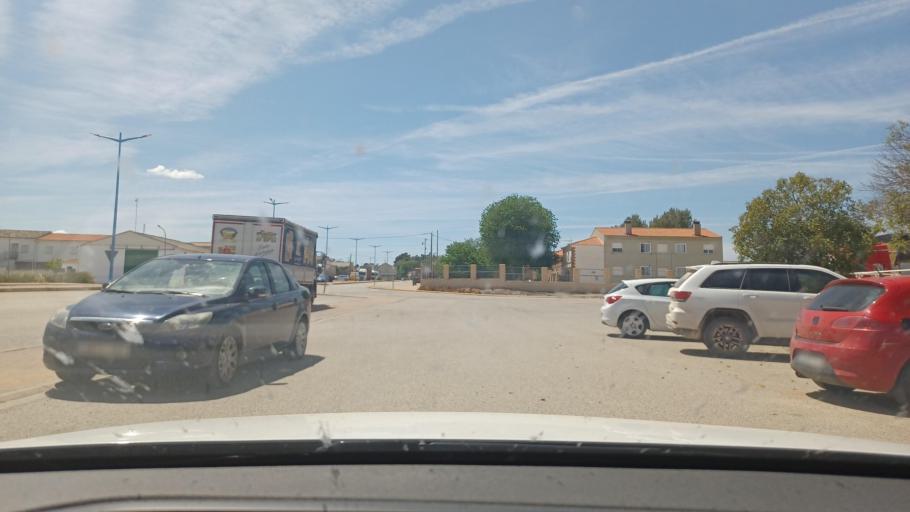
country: ES
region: Castille-La Mancha
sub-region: Provincia de Cuenca
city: Montalbo
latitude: 39.8817
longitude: -2.6652
